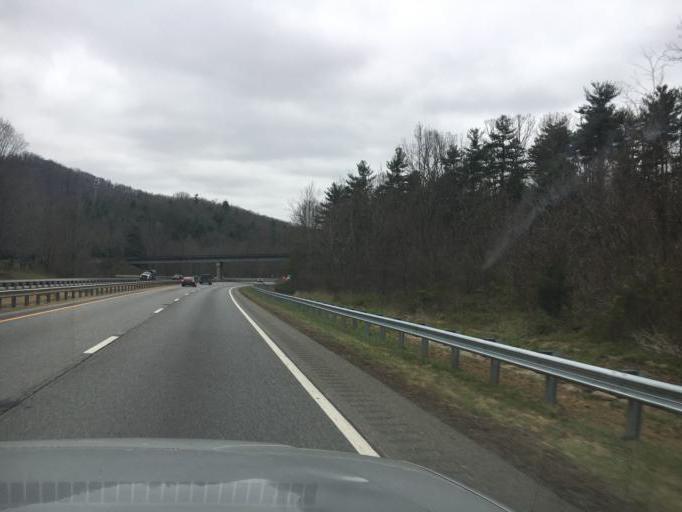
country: US
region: North Carolina
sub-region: Buncombe County
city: Weaverville
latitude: 35.7400
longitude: -82.5456
